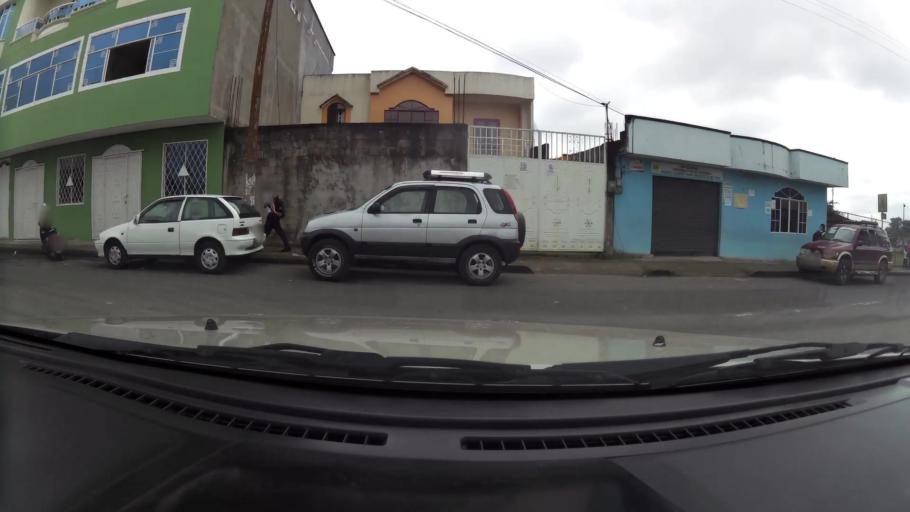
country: EC
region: Santo Domingo de los Tsachilas
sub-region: Canton Santo Domingo de los Colorados
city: Santo Domingo de los Colorados
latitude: -0.2542
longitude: -79.1509
